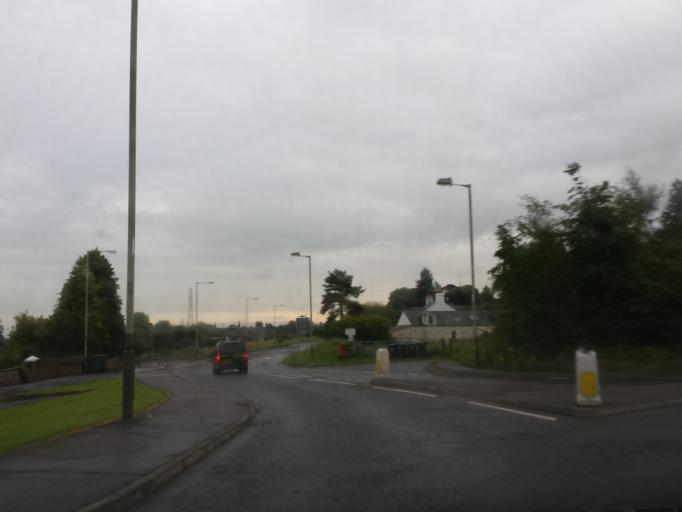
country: GB
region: Scotland
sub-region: Perth and Kinross
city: Abernethy
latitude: 56.3350
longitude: -3.3060
